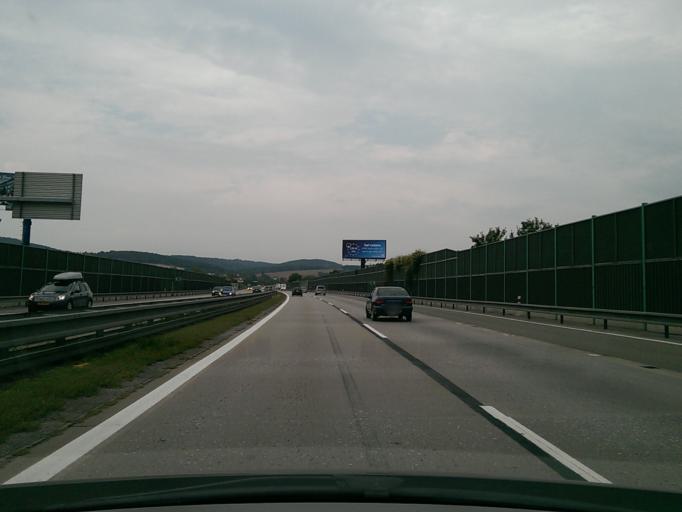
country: CZ
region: South Moravian
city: Troubsko
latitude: 49.1751
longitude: 16.5080
